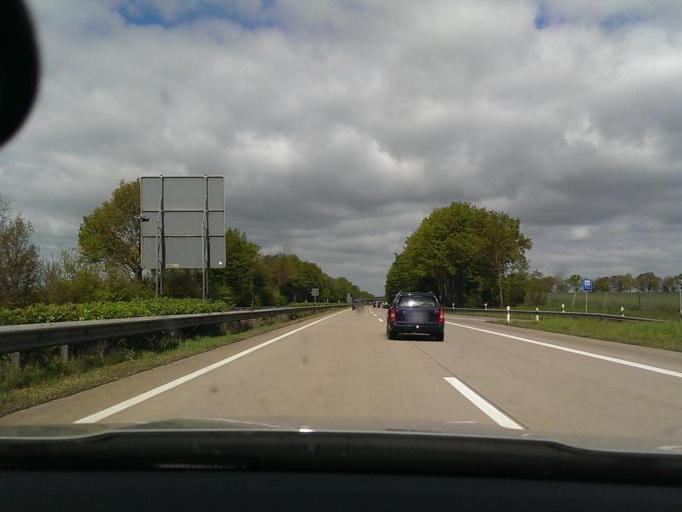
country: DE
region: Lower Saxony
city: Walsrode
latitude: 52.8522
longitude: 9.5565
